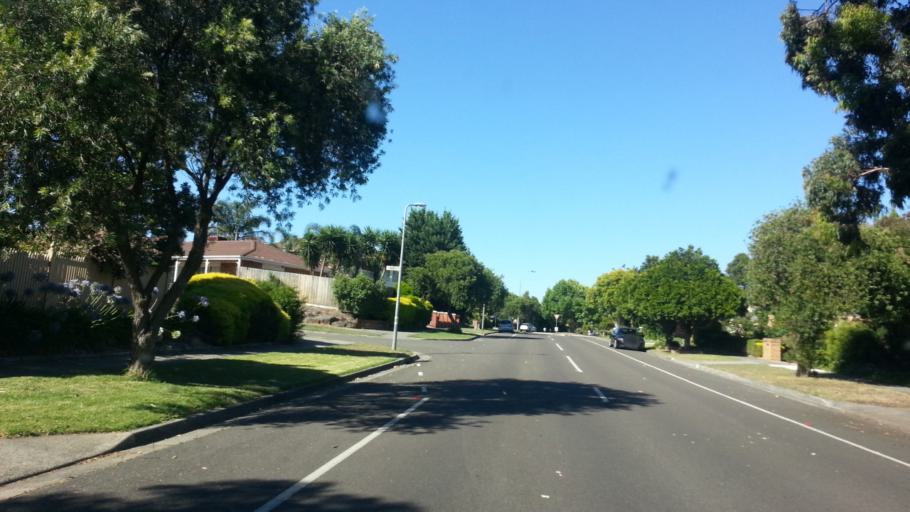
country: AU
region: Victoria
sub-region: Knox
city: Rowville
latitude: -37.9250
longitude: 145.2665
